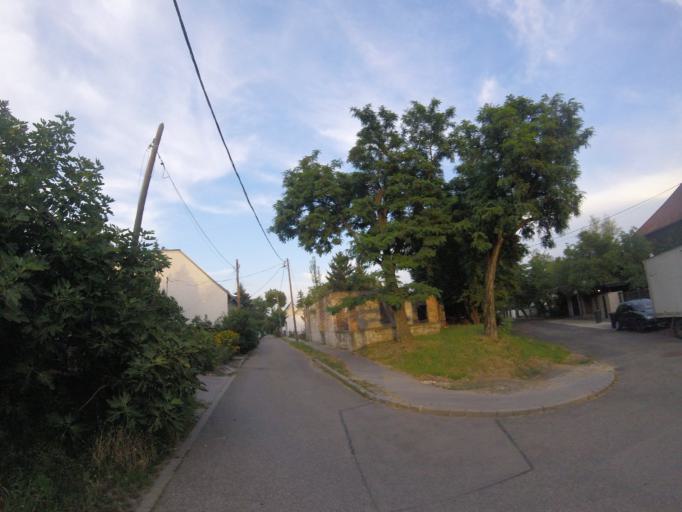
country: HU
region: Pest
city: Budakalasz
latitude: 47.5832
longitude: 19.0498
